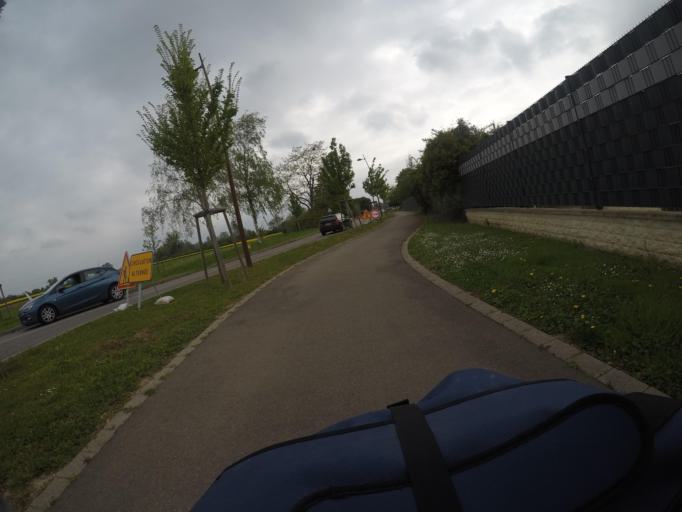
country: FR
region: Alsace
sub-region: Departement du Bas-Rhin
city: Gambsheim
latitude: 48.6897
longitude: 7.8955
